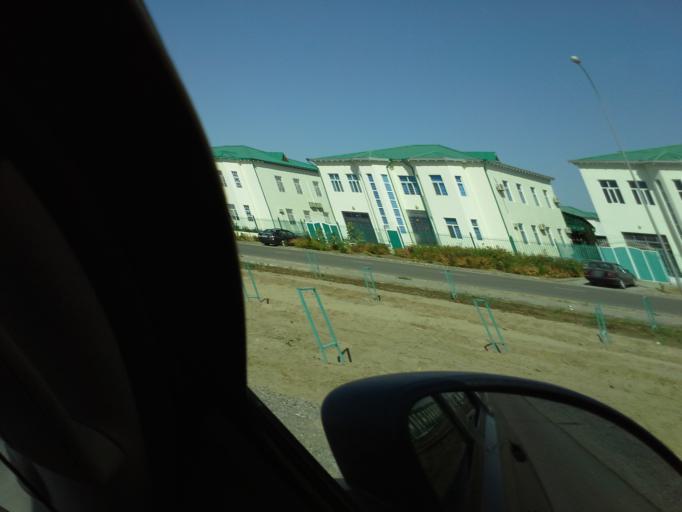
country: TM
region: Dasoguz
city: Dasoguz
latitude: 41.8180
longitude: 59.9521
